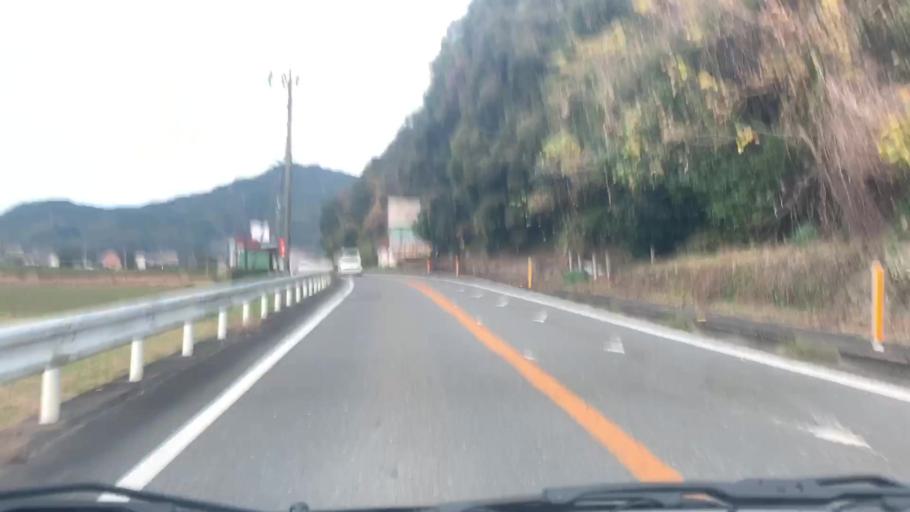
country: JP
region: Saga Prefecture
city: Ureshinomachi-shimojuku
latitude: 33.1347
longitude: 130.0287
